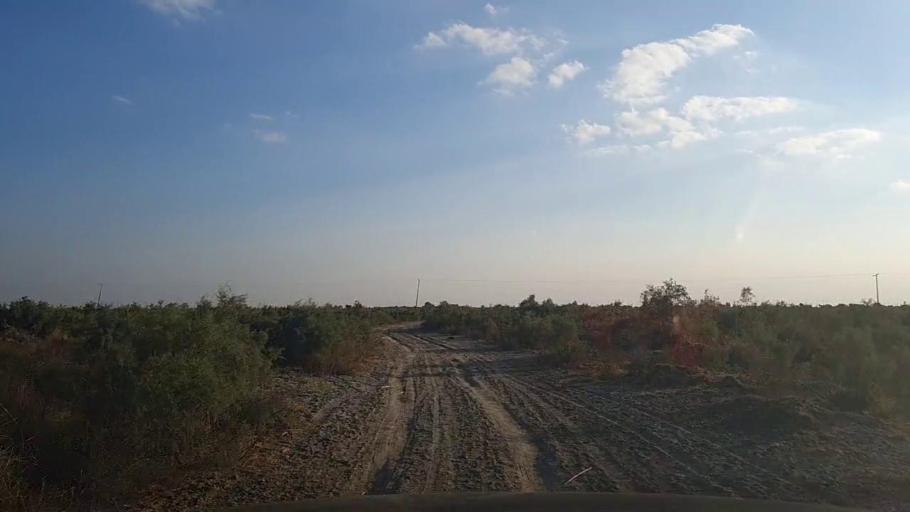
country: PK
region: Sindh
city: Tando Mittha Khan
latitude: 25.9232
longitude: 69.0622
